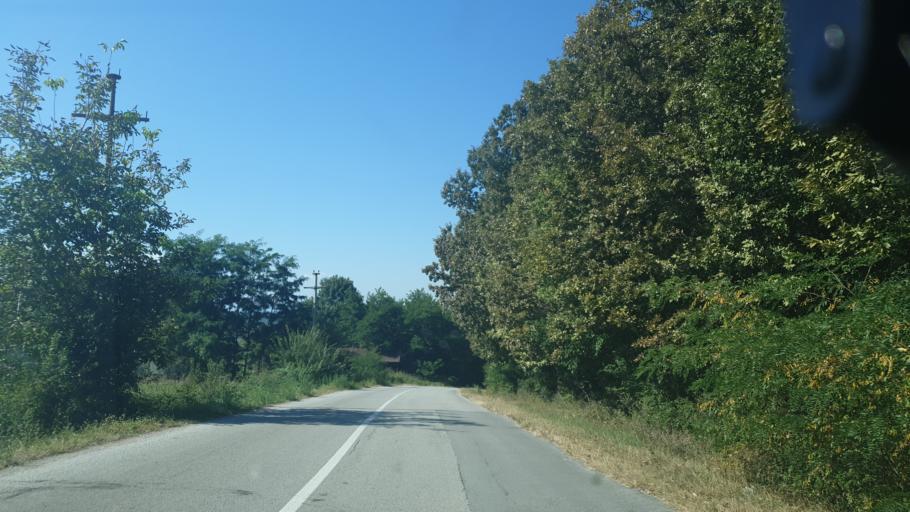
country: RS
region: Central Serbia
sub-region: Kolubarski Okrug
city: Mionica
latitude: 44.2867
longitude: 20.1220
